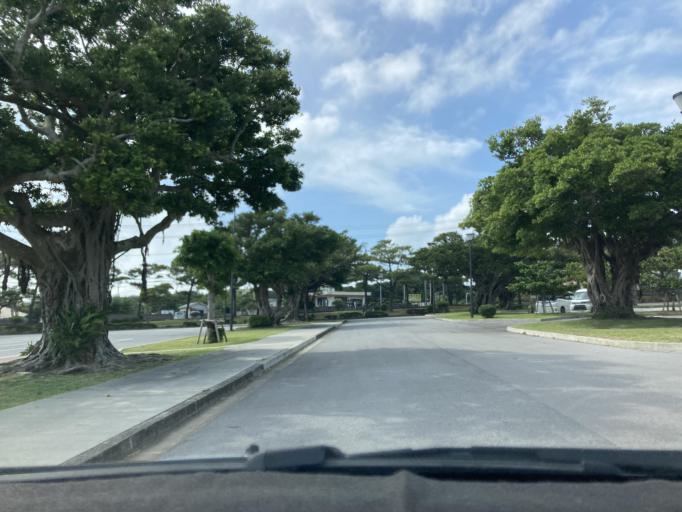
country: JP
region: Okinawa
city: Itoman
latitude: 26.0959
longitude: 127.7223
